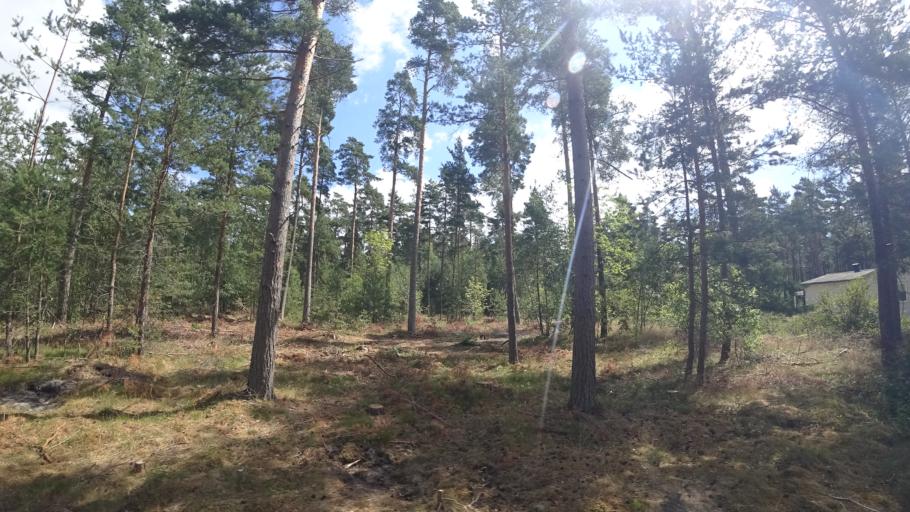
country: SE
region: Skane
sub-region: Kristianstads Kommun
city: Ahus
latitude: 55.9602
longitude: 14.2865
